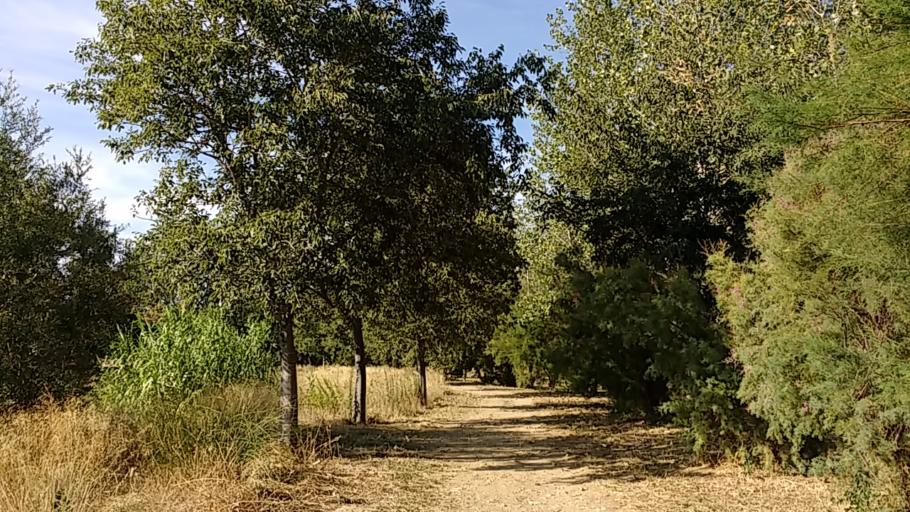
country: FR
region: Languedoc-Roussillon
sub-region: Departement des Pyrenees-Orientales
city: Palau-del-Vidre
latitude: 42.5806
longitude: 2.9611
